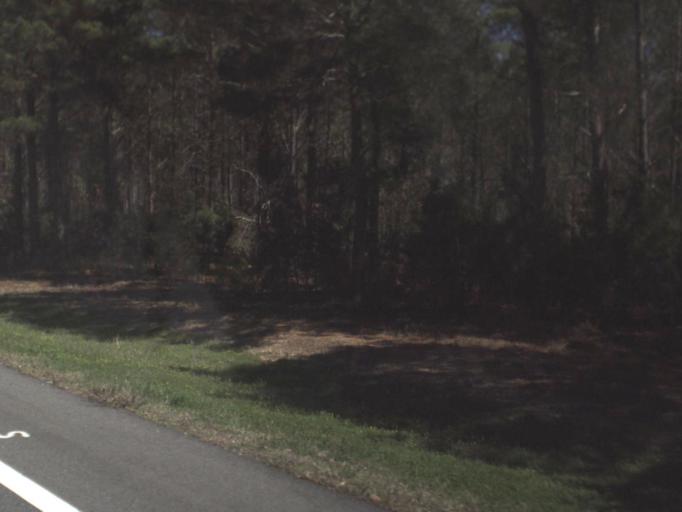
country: US
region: Florida
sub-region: Gadsden County
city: Quincy
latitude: 30.4622
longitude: -84.6395
